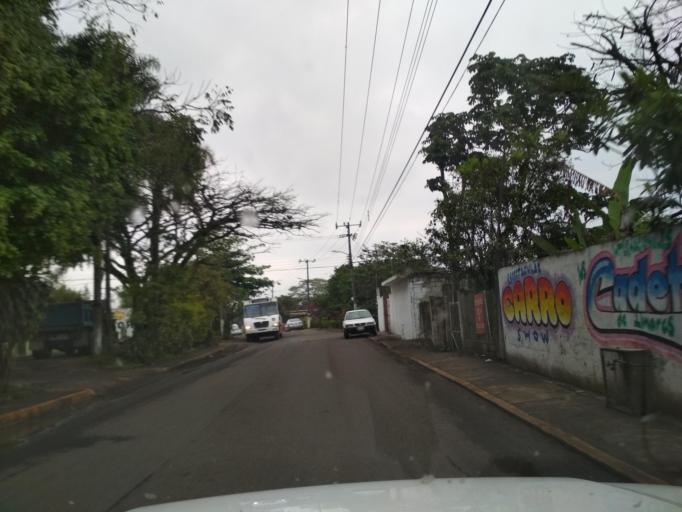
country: MX
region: Veracruz
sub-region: Cordoba
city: Veinte de Noviembre
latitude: 18.8675
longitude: -96.9547
